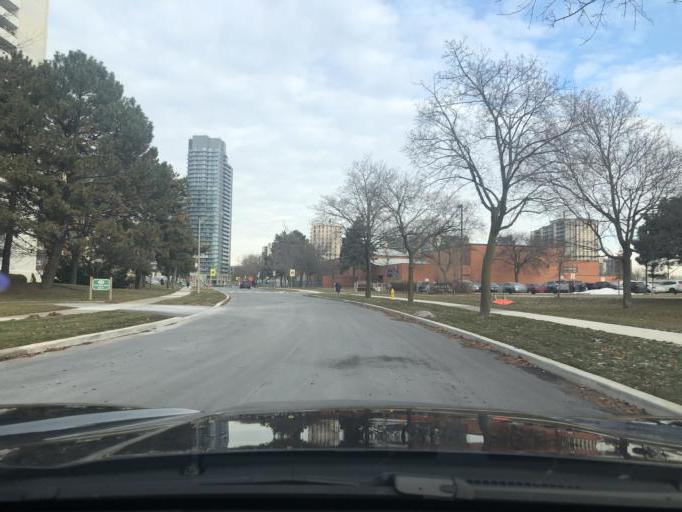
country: CA
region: Ontario
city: Willowdale
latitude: 43.7697
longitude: -79.3436
